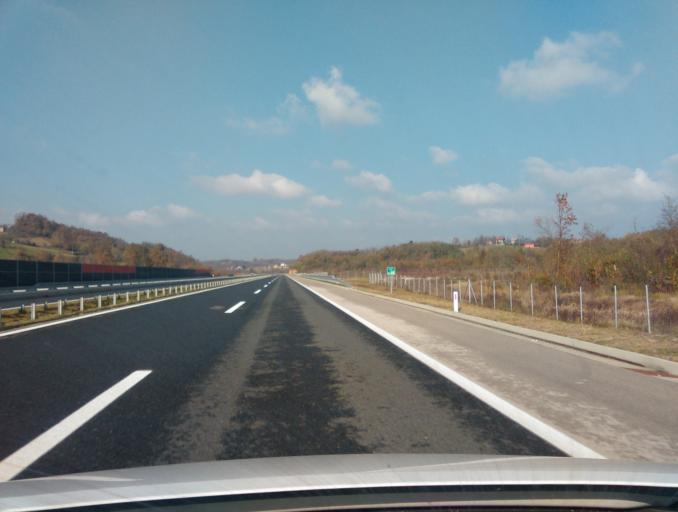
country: BA
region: Republika Srpska
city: Doboj
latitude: 44.8247
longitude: 18.0218
